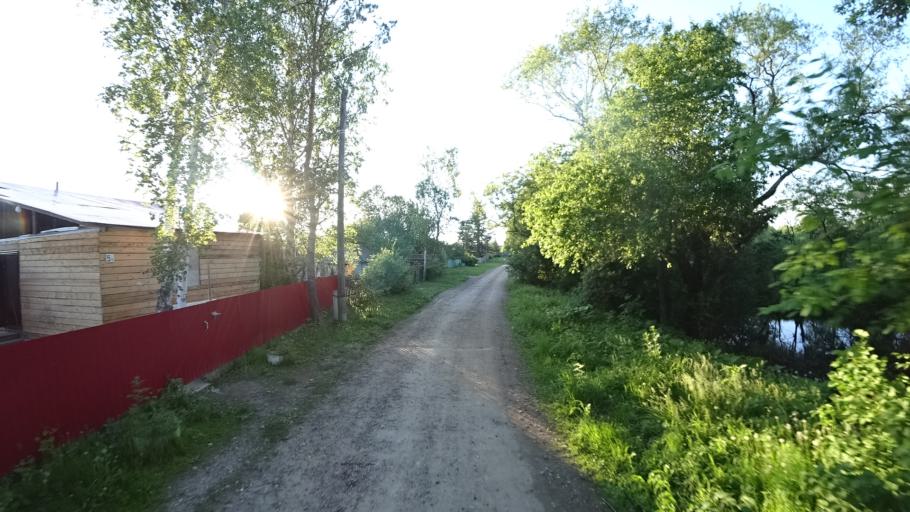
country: RU
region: Khabarovsk Krai
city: Khor
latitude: 47.8545
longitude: 135.0031
